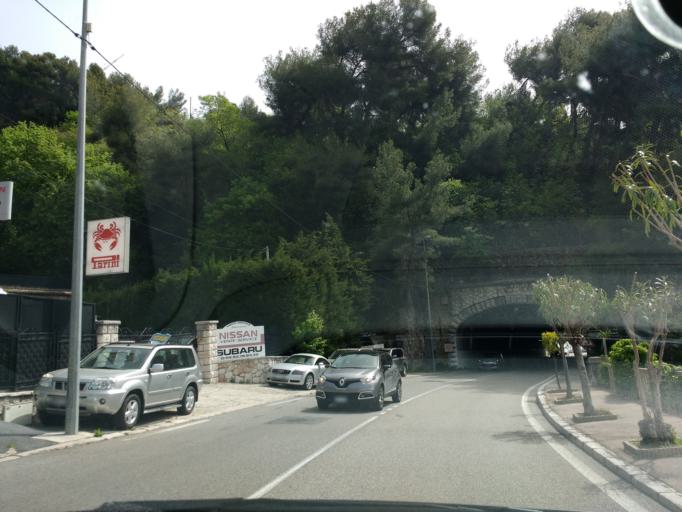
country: MC
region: Commune de Monaco
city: Saint-Roman
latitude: 43.7544
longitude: 7.4352
